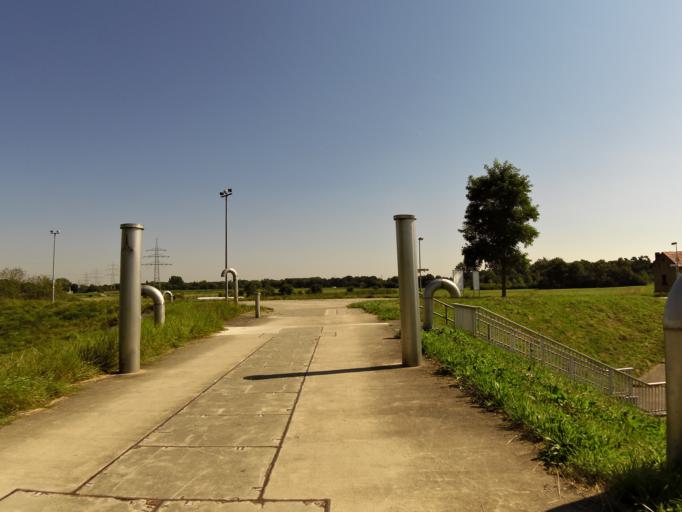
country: DE
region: Hesse
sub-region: Regierungsbezirk Darmstadt
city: Ginsheim-Gustavsburg
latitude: 49.9573
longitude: 8.3567
